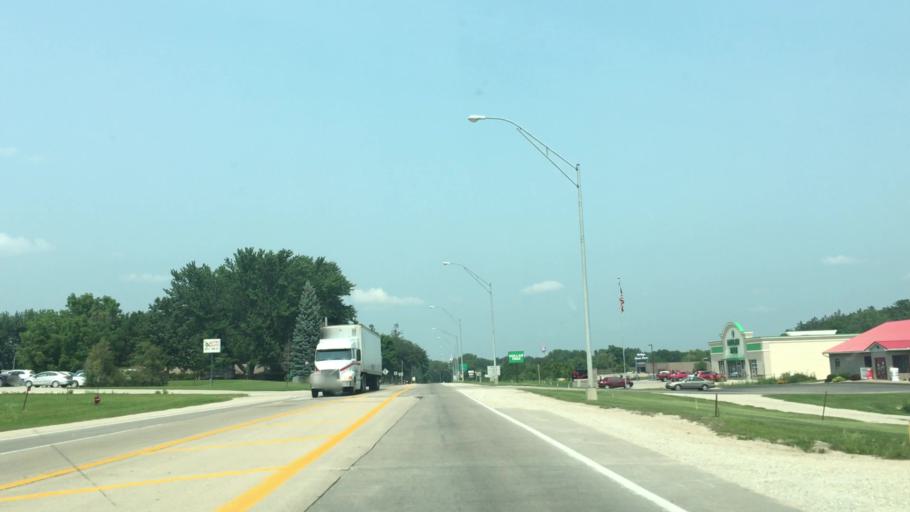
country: US
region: Iowa
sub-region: Buchanan County
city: Independence
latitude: 42.4523
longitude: -91.8902
